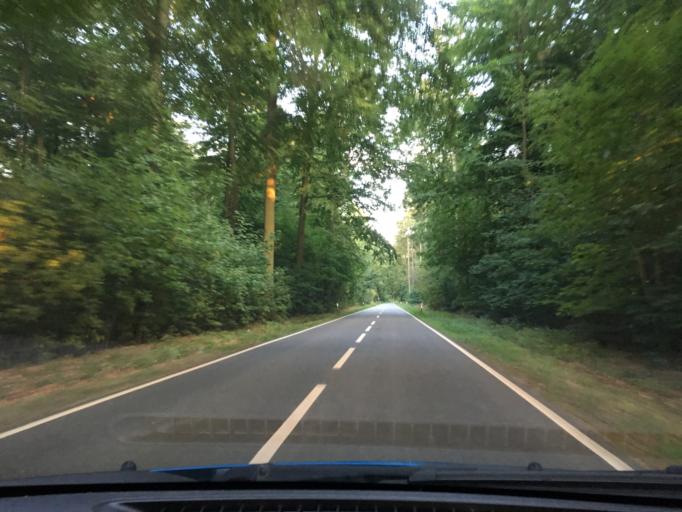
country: DE
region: Lower Saxony
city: Tosterglope
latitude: 53.2312
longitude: 10.7993
